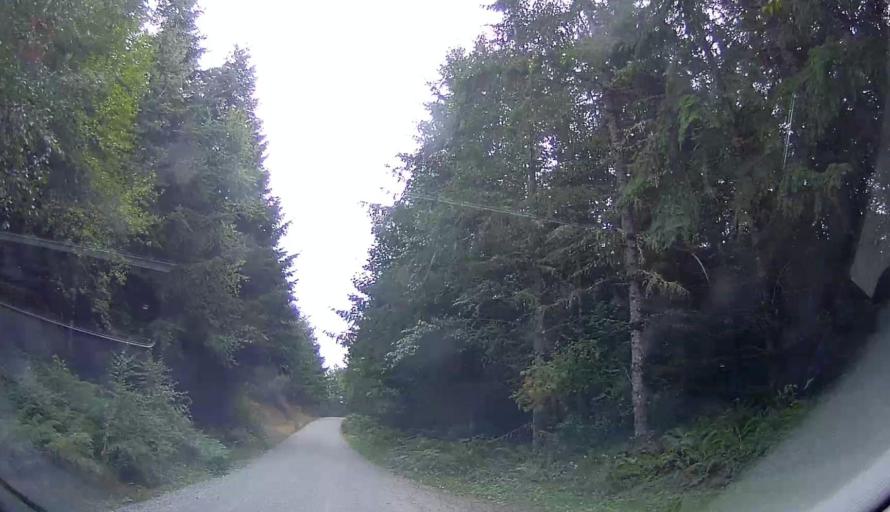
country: US
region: Washington
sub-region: Whatcom County
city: Sudden Valley
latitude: 48.6123
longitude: -122.4170
